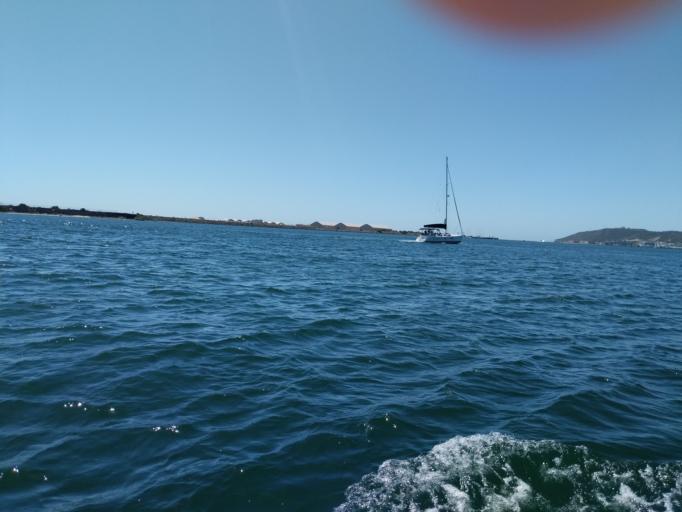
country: US
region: California
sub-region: San Diego County
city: Coronado
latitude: 32.7097
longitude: -117.2258
